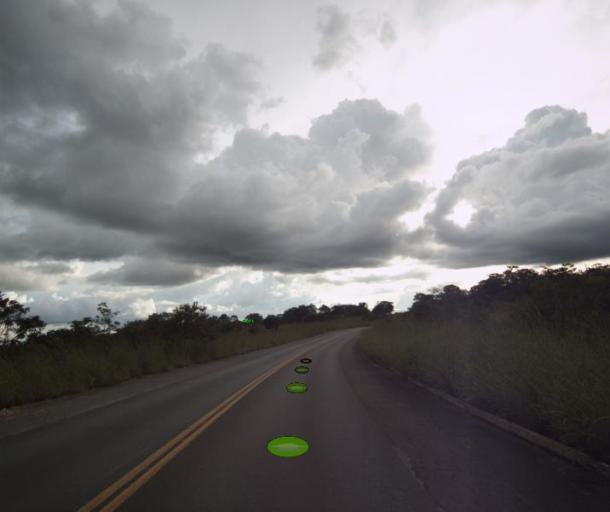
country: BR
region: Goias
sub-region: Niquelandia
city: Niquelandia
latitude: -14.4997
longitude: -48.4954
